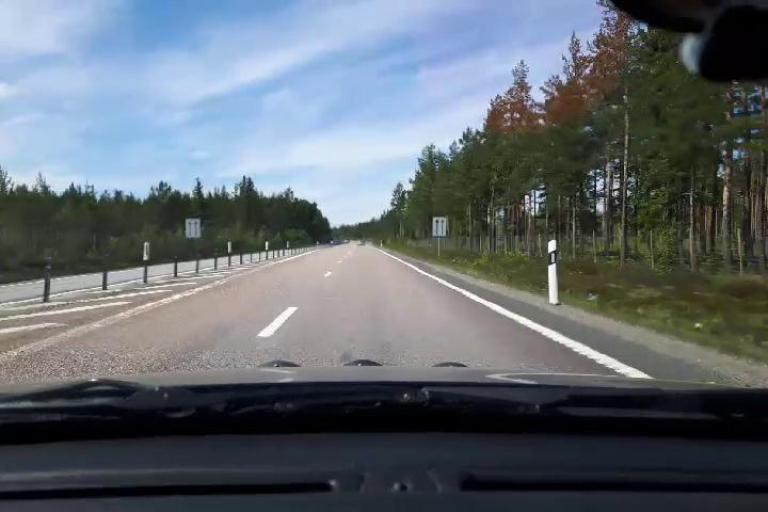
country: SE
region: Gaevleborg
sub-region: Gavle Kommun
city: Norrsundet
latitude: 60.9840
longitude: 17.0139
